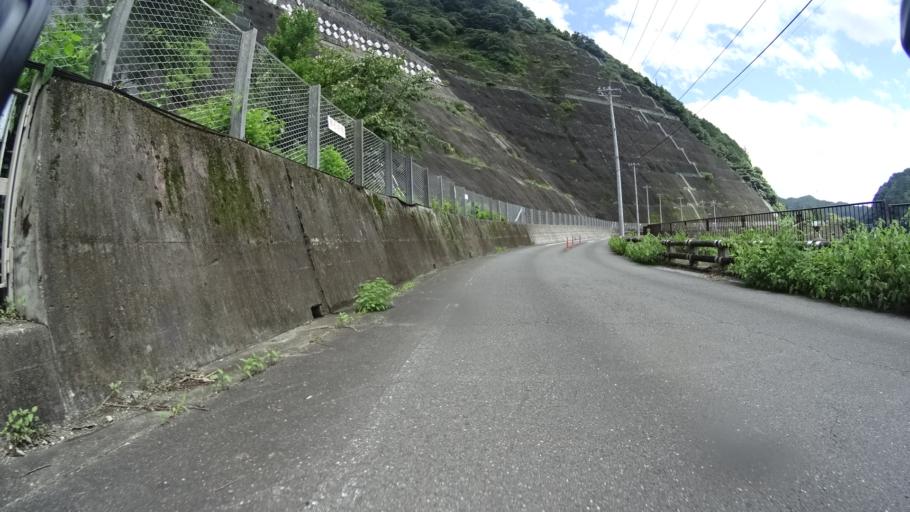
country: JP
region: Tokyo
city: Ome
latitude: 35.8758
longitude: 139.1683
